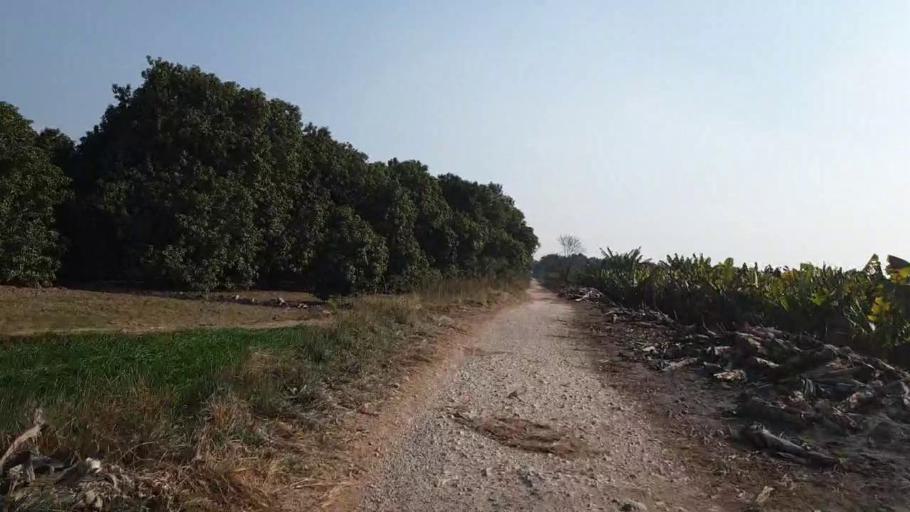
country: PK
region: Sindh
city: Tando Adam
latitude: 25.6066
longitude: 68.6140
